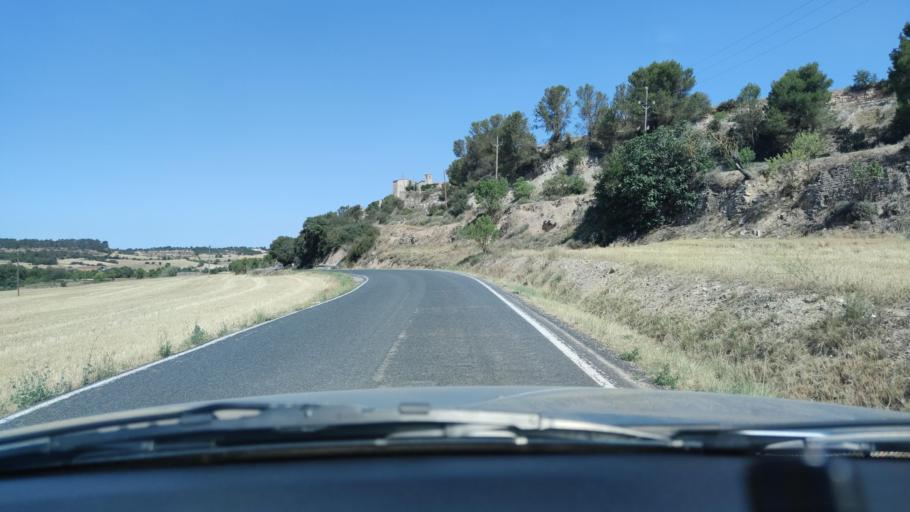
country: ES
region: Catalonia
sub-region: Provincia de Lleida
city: Sant Guim de Freixenet
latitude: 41.6738
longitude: 1.3594
